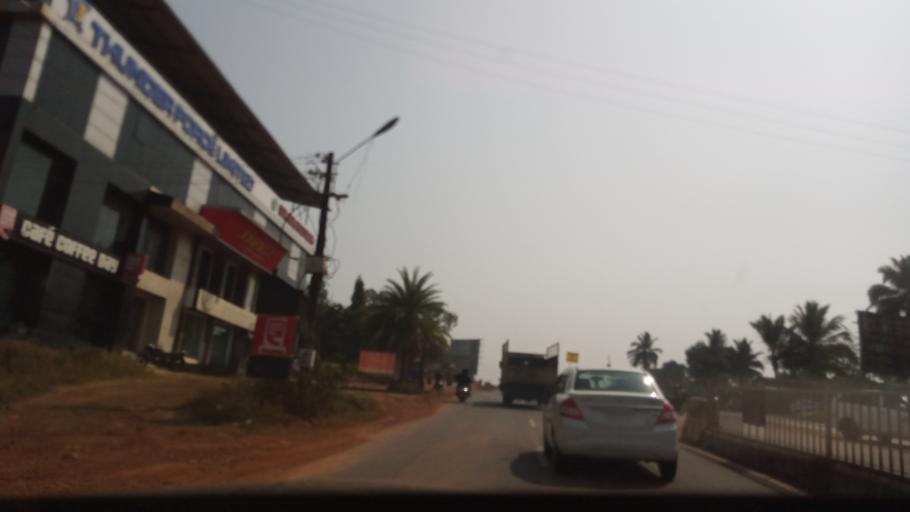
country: IN
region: Goa
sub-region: North Goa
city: Bambolim
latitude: 15.4647
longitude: 73.8539
